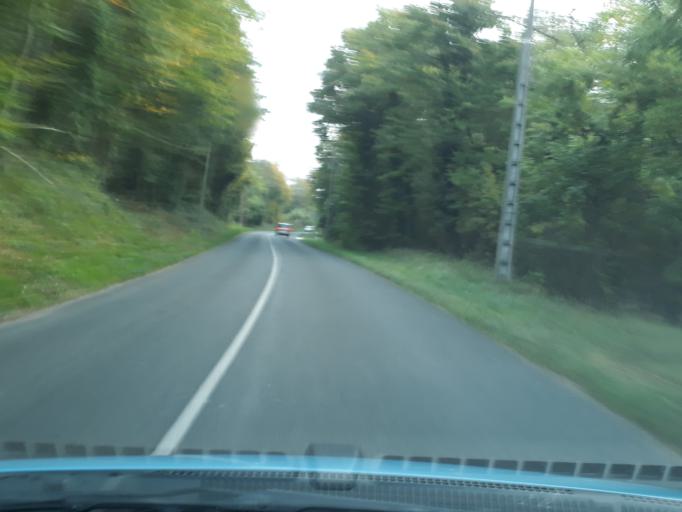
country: FR
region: Ile-de-France
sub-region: Departement de Seine-et-Marne
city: Veneux-les-Sablons
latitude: 48.3581
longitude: 2.8004
